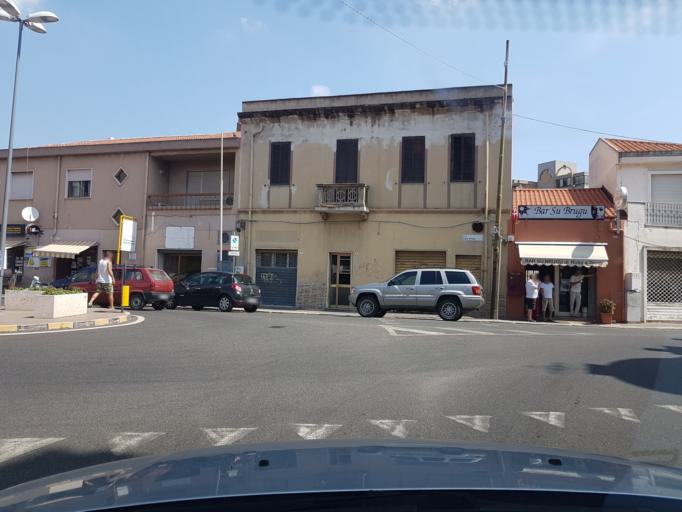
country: IT
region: Sardinia
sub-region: Provincia di Oristano
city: Oristano
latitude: 39.9025
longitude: 8.5991
